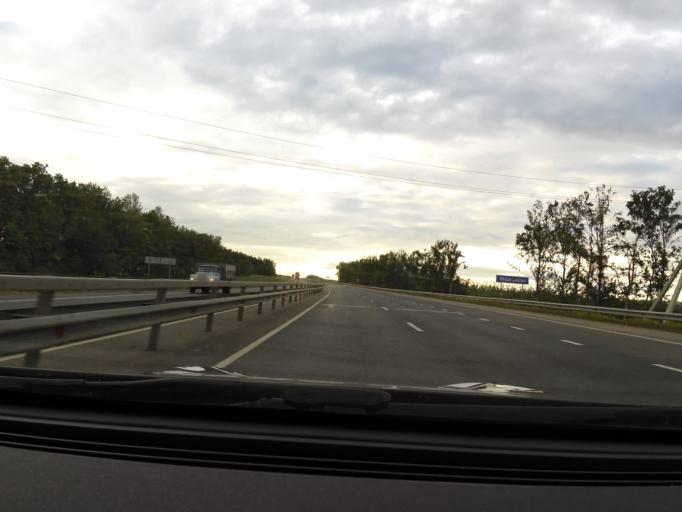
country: RU
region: Chuvashia
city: Tsivil'sk
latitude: 55.9358
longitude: 47.3905
